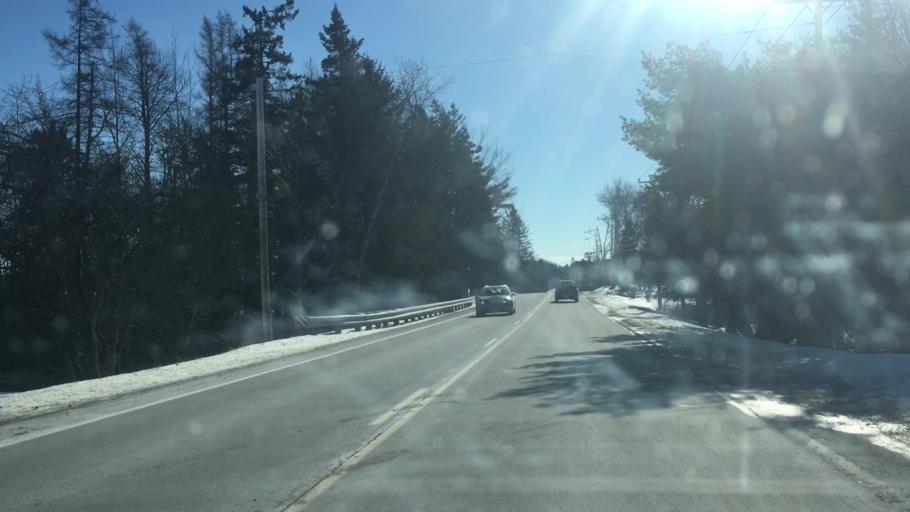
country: US
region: Maine
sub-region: Hancock County
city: Ellsworth
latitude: 44.5262
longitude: -68.4318
